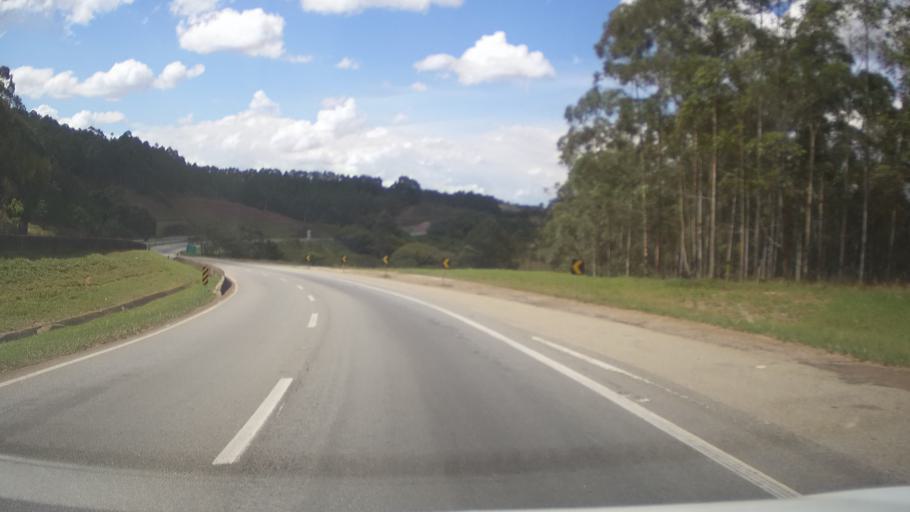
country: BR
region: Minas Gerais
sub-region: Santo Antonio Do Amparo
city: Santo Antonio do Amparo
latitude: -20.8585
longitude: -44.8365
